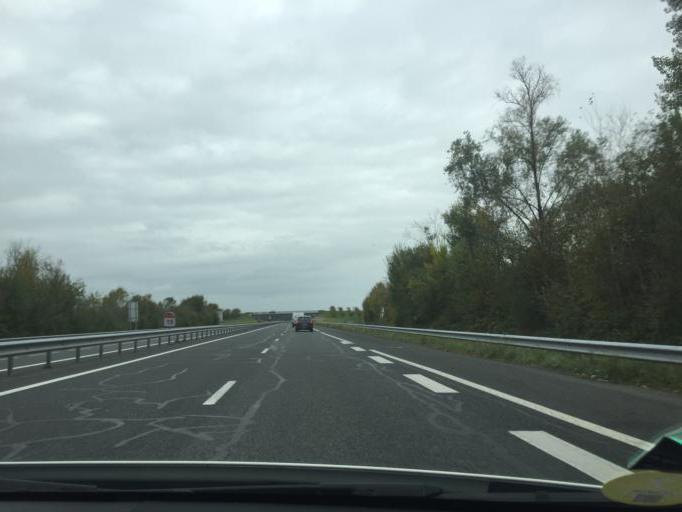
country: FR
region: Bourgogne
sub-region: Departement de l'Yonne
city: Egriselles-le-Bocage
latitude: 48.1712
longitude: 3.1767
